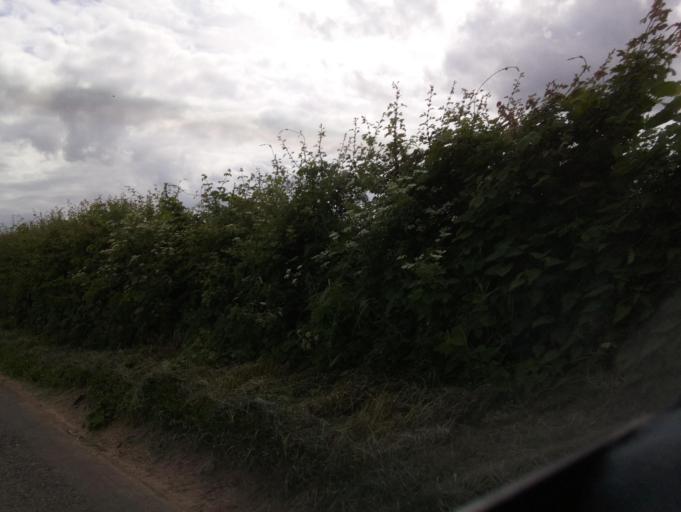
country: GB
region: England
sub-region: Herefordshire
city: Ledbury
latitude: 52.0785
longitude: -2.4567
